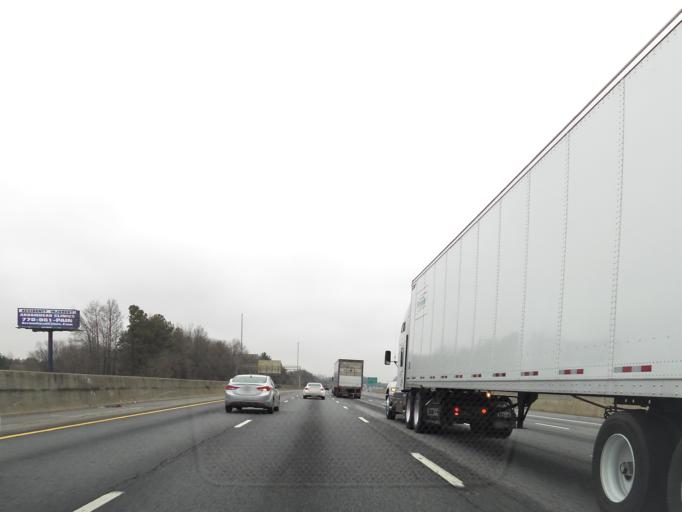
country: US
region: Georgia
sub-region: Clayton County
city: Forest Park
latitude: 33.5982
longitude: -84.3898
